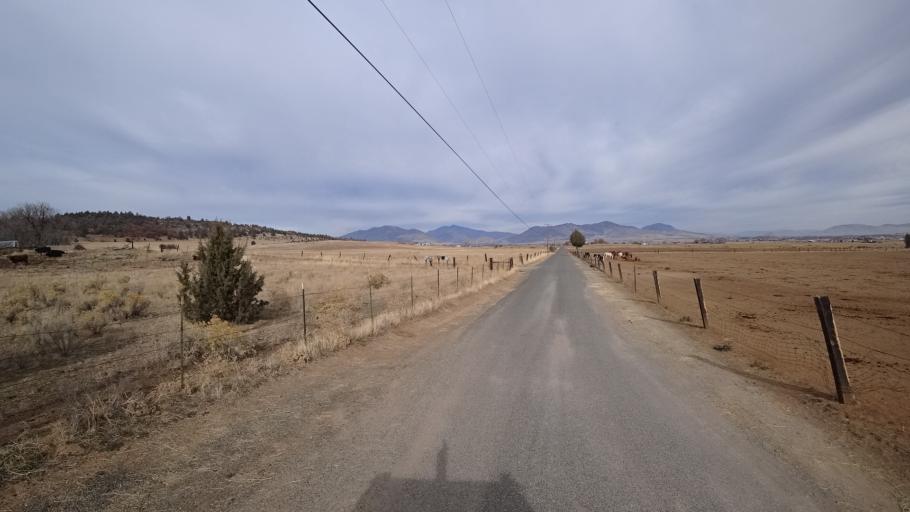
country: US
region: California
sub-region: Siskiyou County
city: Montague
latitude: 41.6940
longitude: -122.5638
